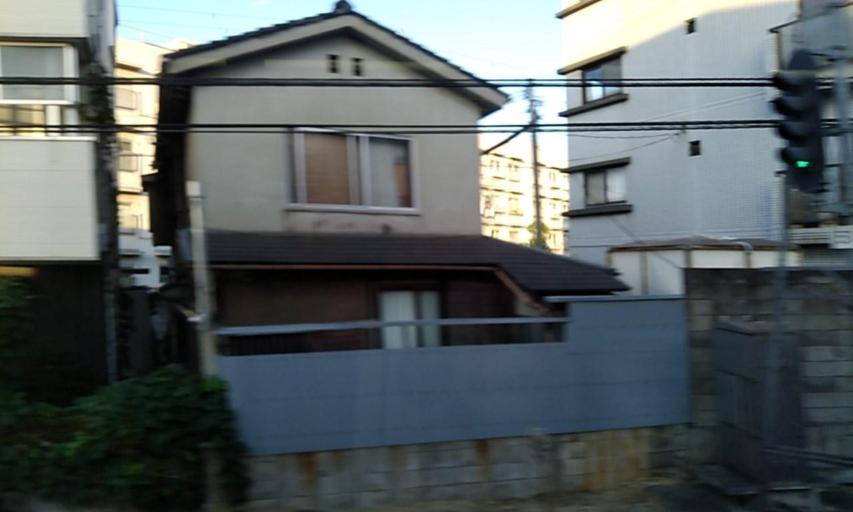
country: JP
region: Osaka
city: Sakai
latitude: 34.6266
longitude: 135.4975
